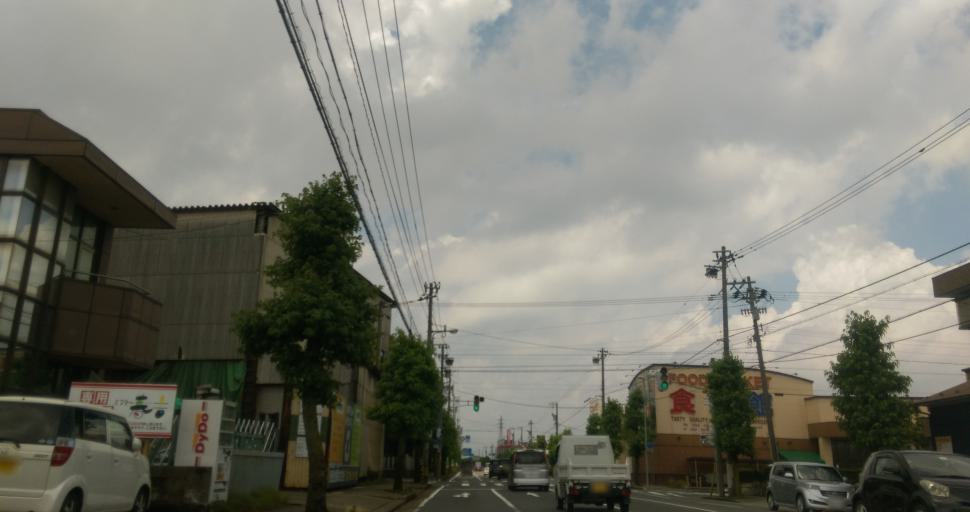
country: JP
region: Fukui
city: Fukui-shi
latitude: 36.0787
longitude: 136.1975
